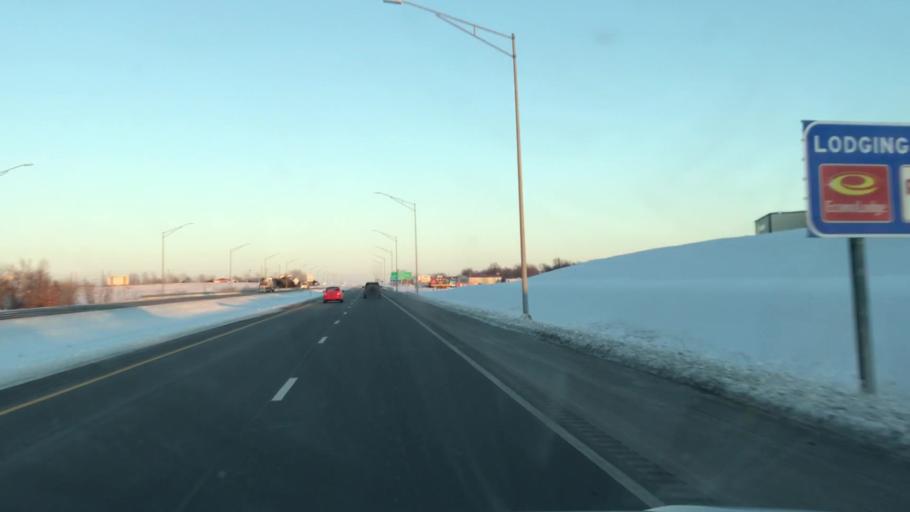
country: US
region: Missouri
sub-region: Clinton County
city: Cameron
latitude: 39.7539
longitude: -94.2504
